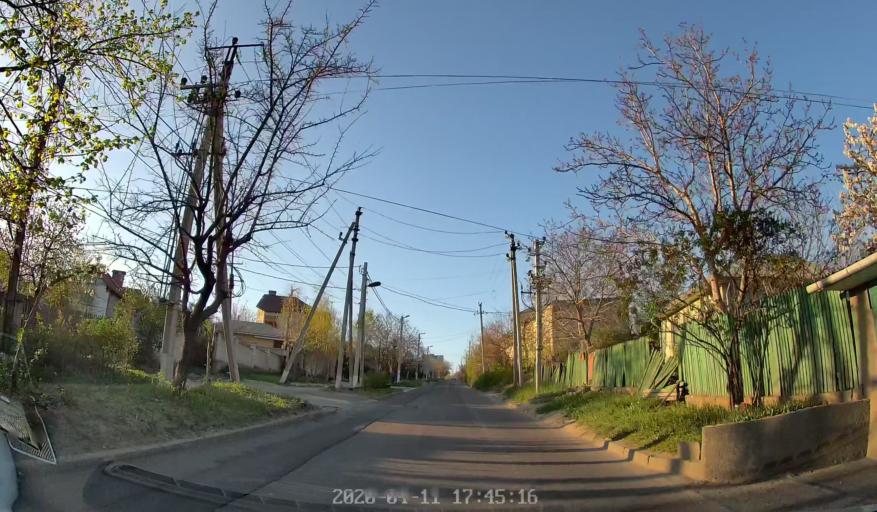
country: MD
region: Chisinau
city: Chisinau
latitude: 46.9836
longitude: 28.8228
